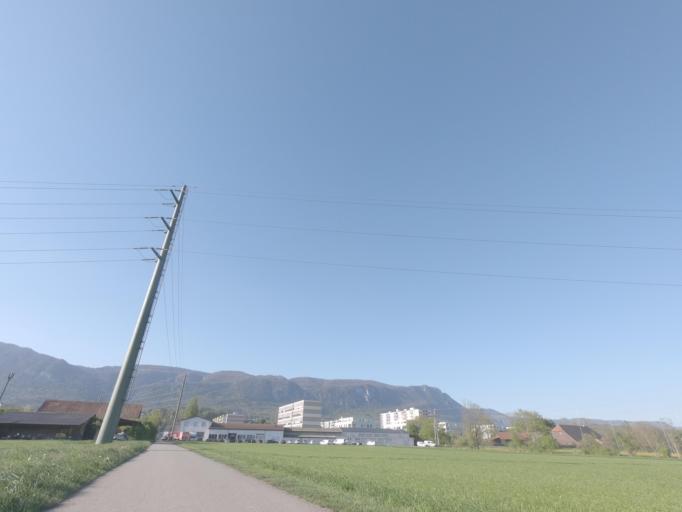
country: CH
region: Solothurn
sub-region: Bezirk Lebern
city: Langendorf
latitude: 47.2071
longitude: 7.5083
